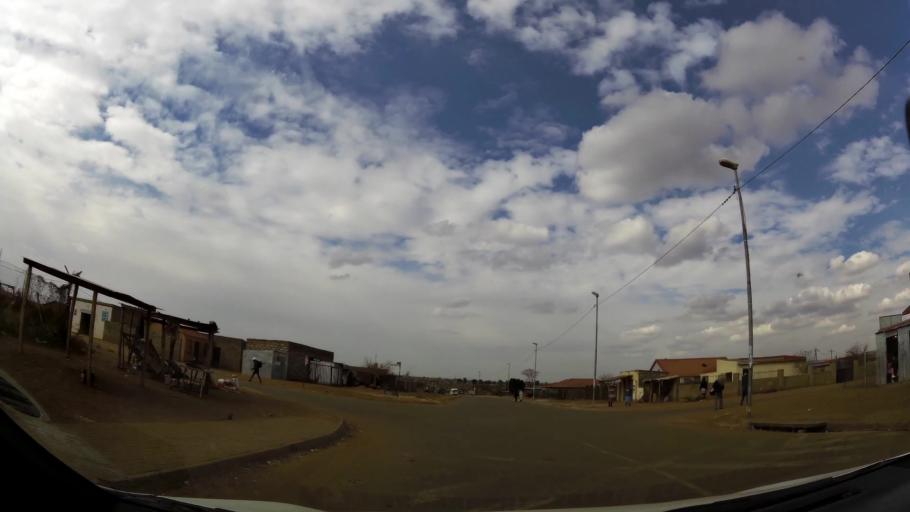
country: ZA
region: Gauteng
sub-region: Ekurhuleni Metropolitan Municipality
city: Germiston
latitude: -26.4084
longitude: 28.1609
